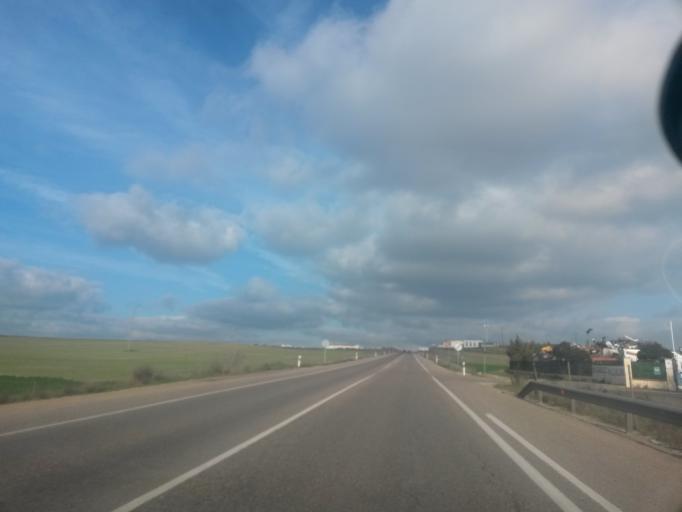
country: ES
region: Castille and Leon
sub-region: Provincia de Salamanca
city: San Cristobal de la Cuesta
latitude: 41.0041
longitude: -5.6210
